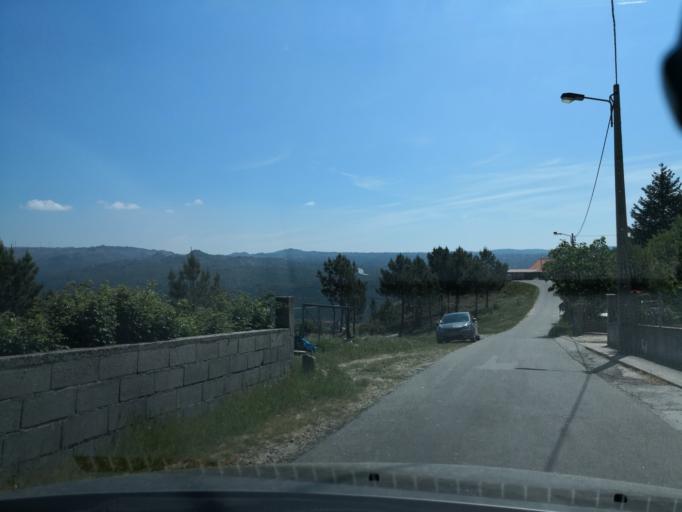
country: PT
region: Vila Real
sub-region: Vila Real
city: Vila Real
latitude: 41.3619
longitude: -7.7329
